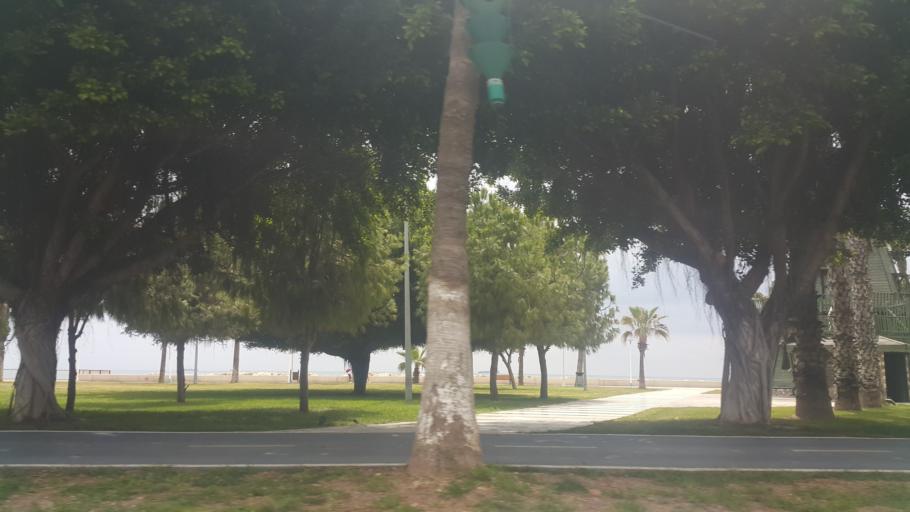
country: TR
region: Mersin
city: Mercin
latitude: 36.7674
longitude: 34.5595
